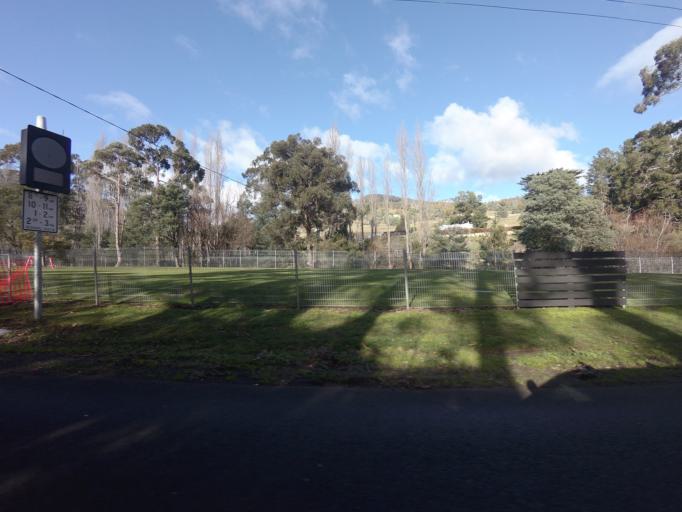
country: AU
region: Tasmania
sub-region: Glenorchy
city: Granton
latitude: -42.8041
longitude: 147.1549
